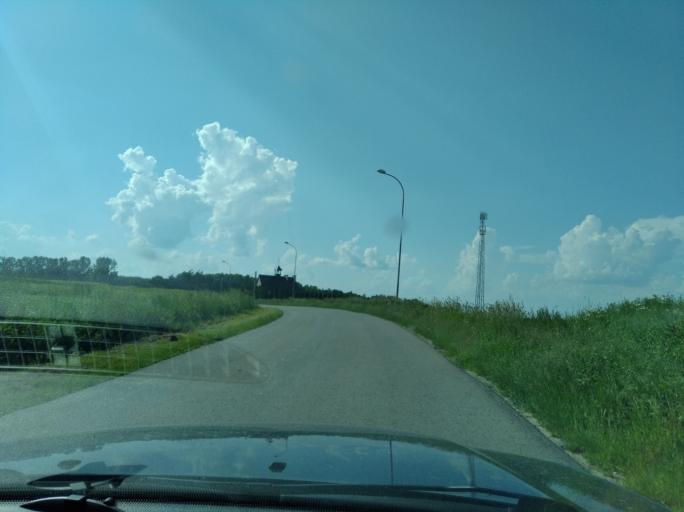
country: PL
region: Subcarpathian Voivodeship
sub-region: Powiat jaroslawski
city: Rokietnica
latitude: 49.9273
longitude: 22.6827
